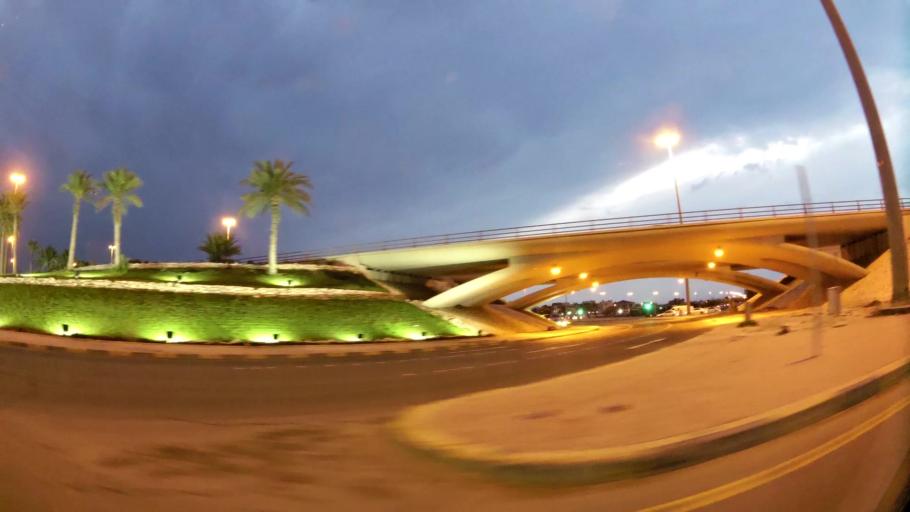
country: BH
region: Central Governorate
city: Madinat Hamad
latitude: 26.1403
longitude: 50.5111
